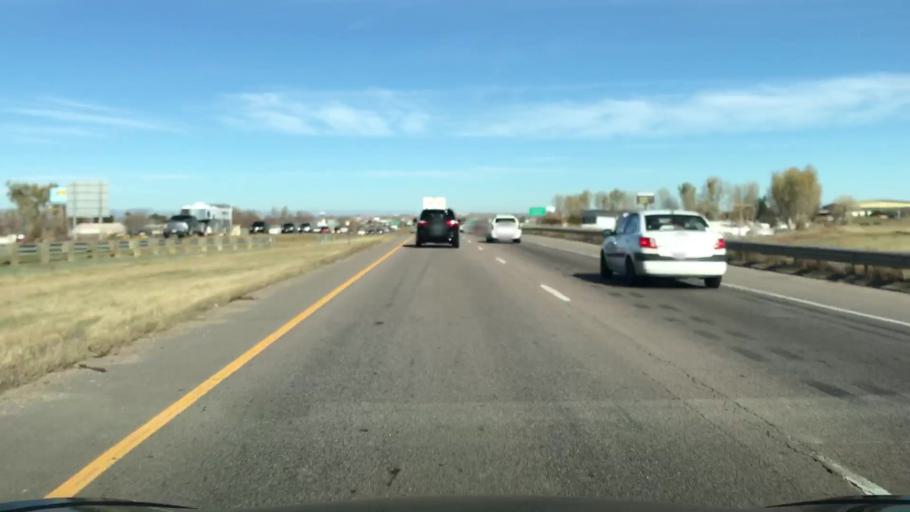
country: US
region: Colorado
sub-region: Weld County
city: Johnstown
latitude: 40.3497
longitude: -104.9810
